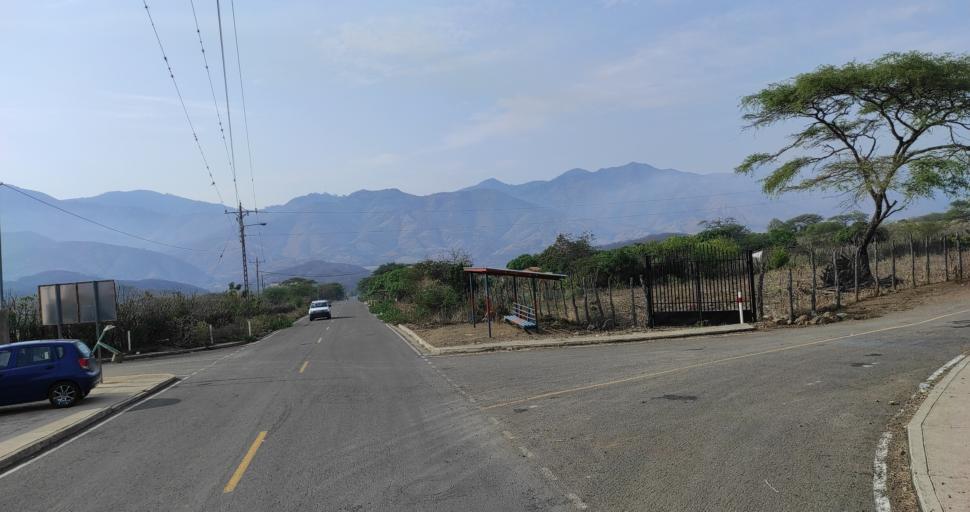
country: EC
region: Loja
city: Catacocha
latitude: -4.0076
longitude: -79.6976
